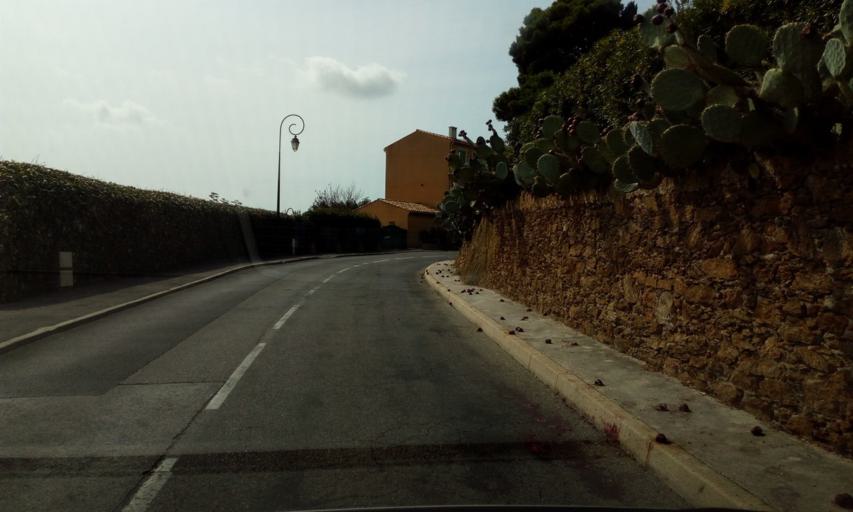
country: FR
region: Provence-Alpes-Cote d'Azur
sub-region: Departement du Var
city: Bormes-les-Mimosas
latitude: 43.1491
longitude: 6.3429
